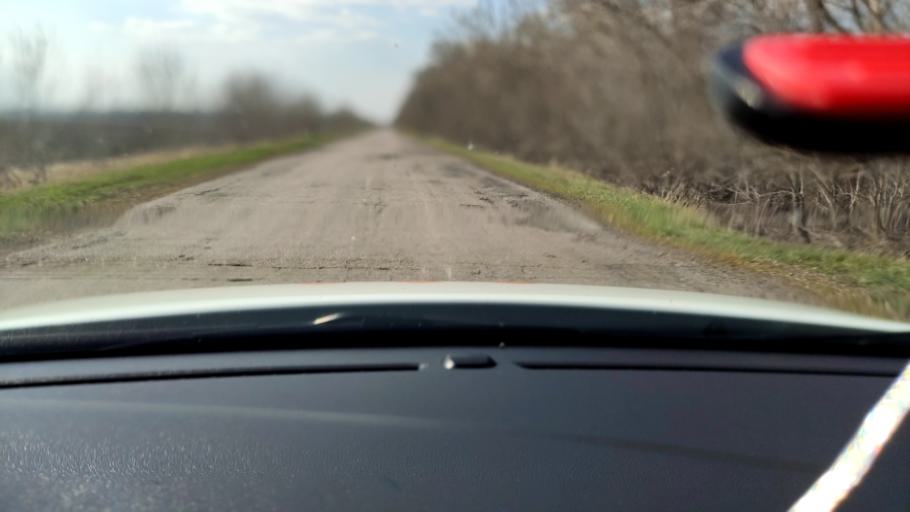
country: RU
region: Voronezj
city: Uryv-Pokrovka
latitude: 51.1413
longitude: 39.0745
